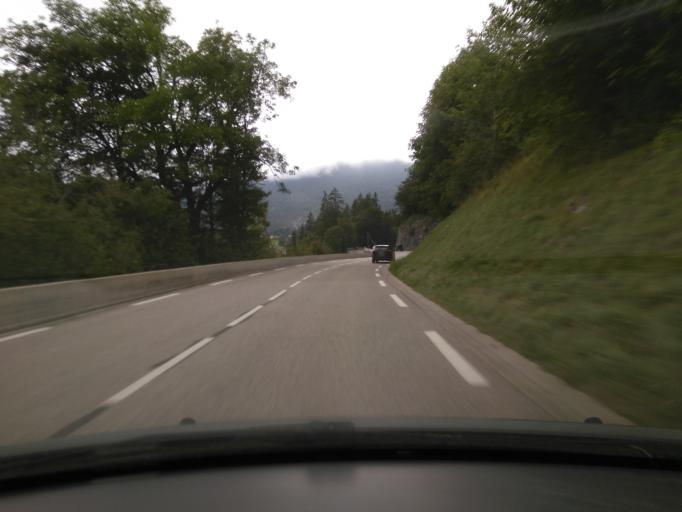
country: FR
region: Rhone-Alpes
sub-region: Departement de la Haute-Savoie
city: Saint-Jean-de-Sixt
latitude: 45.9181
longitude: 6.4176
